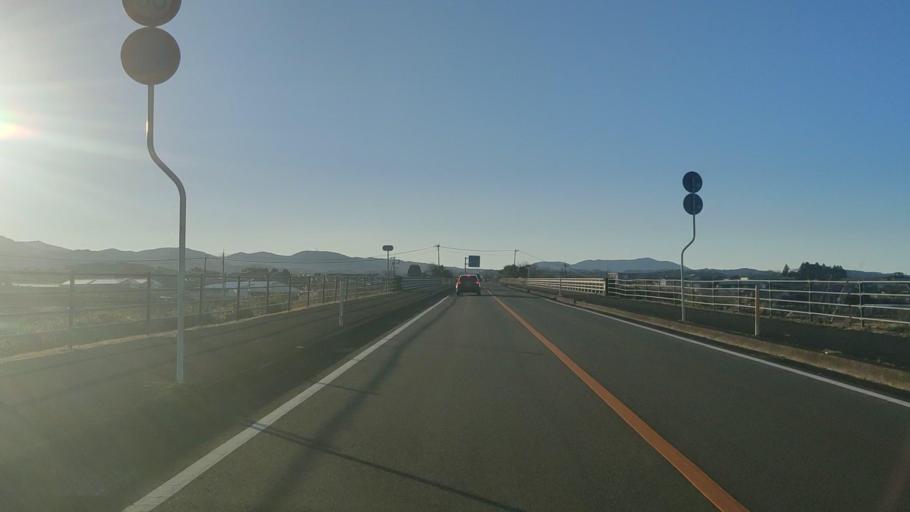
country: JP
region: Miyazaki
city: Miyazaki-shi
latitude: 31.8312
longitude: 131.3071
